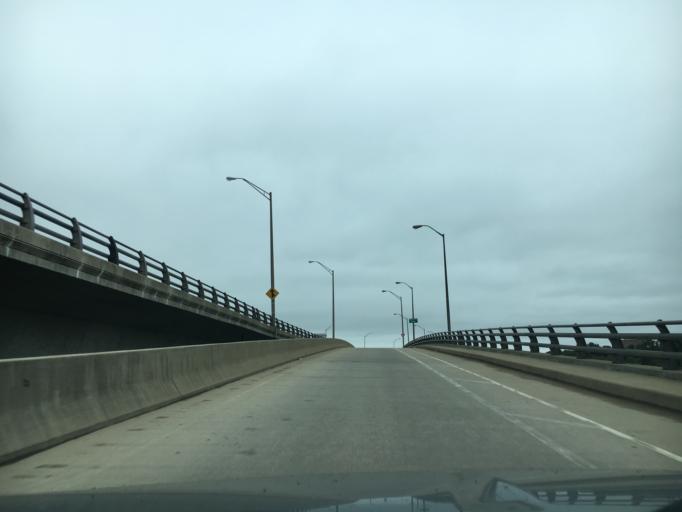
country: US
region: Virginia
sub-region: City of Richmond
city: Richmond
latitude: 37.5349
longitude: -77.4495
